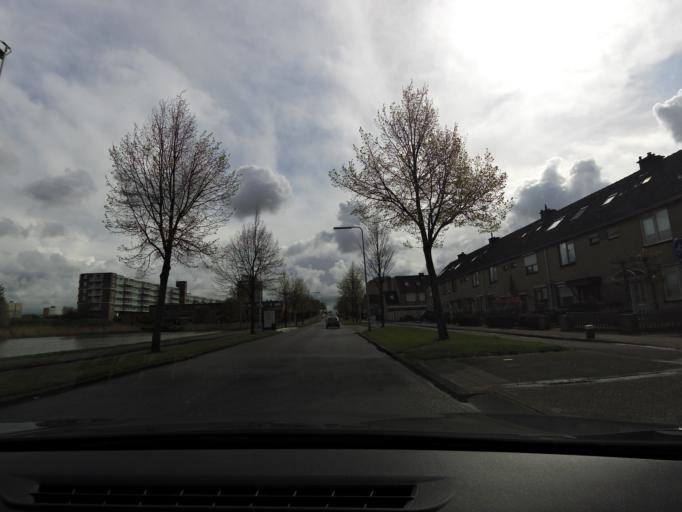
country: NL
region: South Holland
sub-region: Gemeente Spijkenisse
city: Spijkenisse
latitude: 51.8472
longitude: 4.3447
